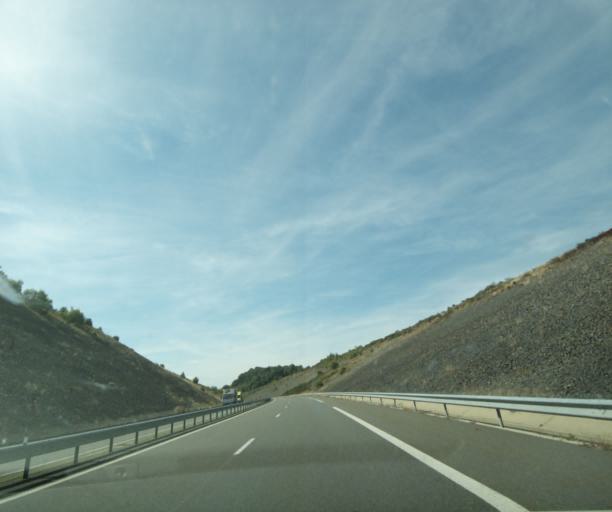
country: FR
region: Auvergne
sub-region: Departement du Puy-de-Dome
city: Chapdes-Beaufort
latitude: 45.8530
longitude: 2.8456
